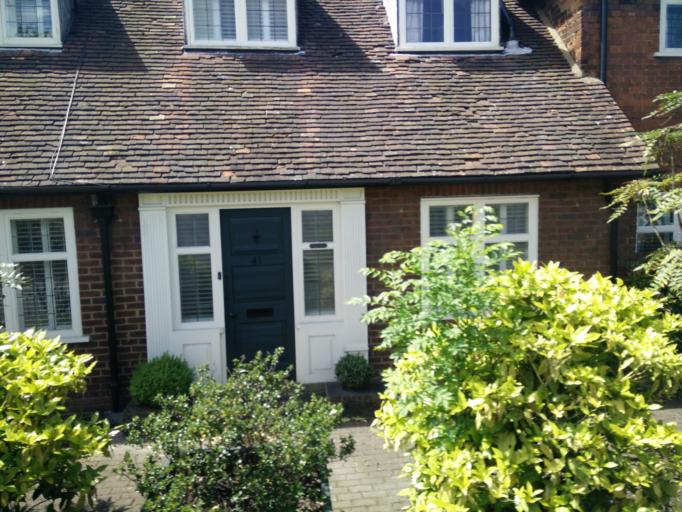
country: GB
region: England
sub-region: Hertfordshire
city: Hitchin
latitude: 51.9474
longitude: -0.2826
